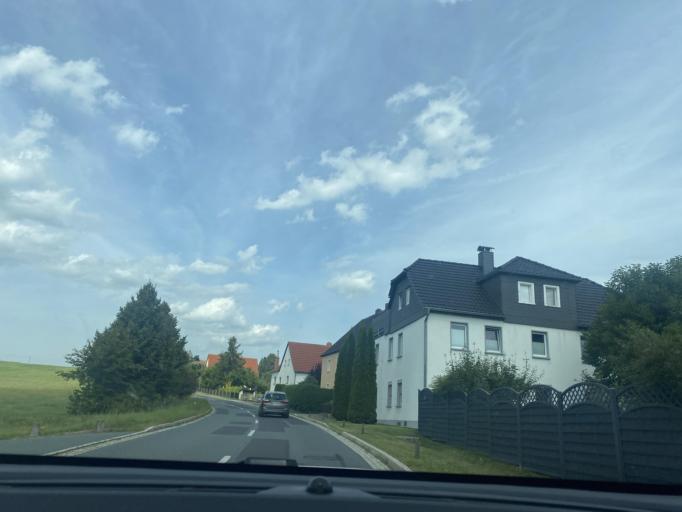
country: DE
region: Saxony
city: Mittelherwigsdorf
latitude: 50.9582
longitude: 14.7335
